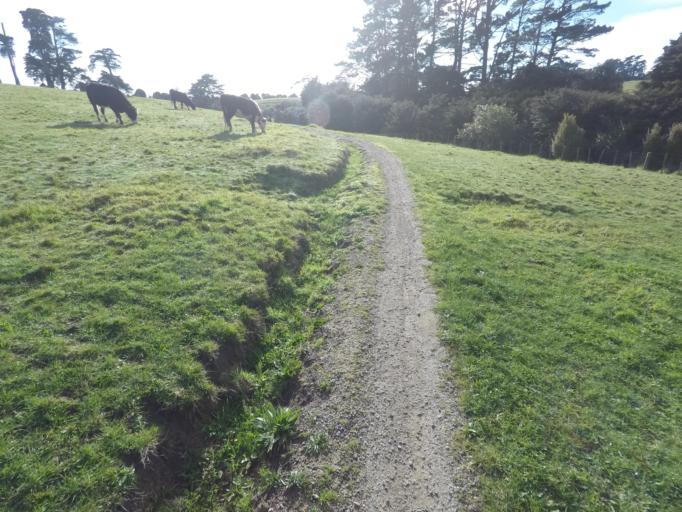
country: NZ
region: Auckland
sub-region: Auckland
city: Manukau City
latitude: -36.9923
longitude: 174.9112
